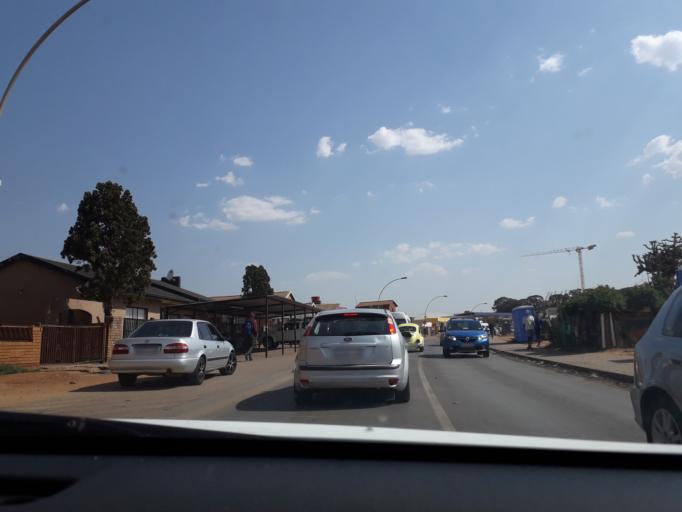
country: ZA
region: Gauteng
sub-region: Ekurhuleni Metropolitan Municipality
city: Tembisa
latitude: -26.0190
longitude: 28.2305
